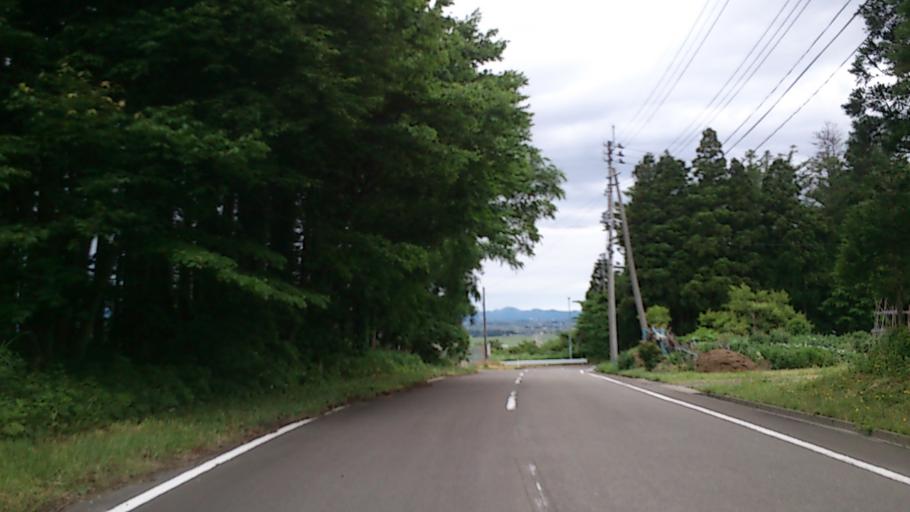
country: JP
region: Yamagata
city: Tsuruoka
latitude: 38.7834
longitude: 139.9748
